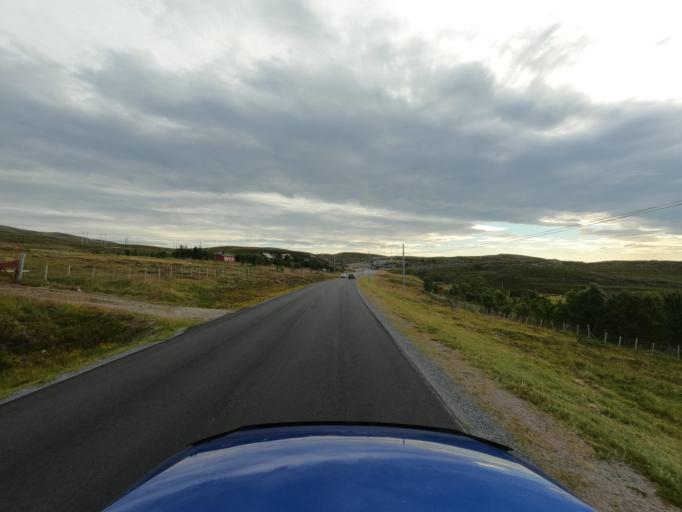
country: NO
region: Finnmark Fylke
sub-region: Hammerfest
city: Rypefjord
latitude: 70.5428
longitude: 23.7343
